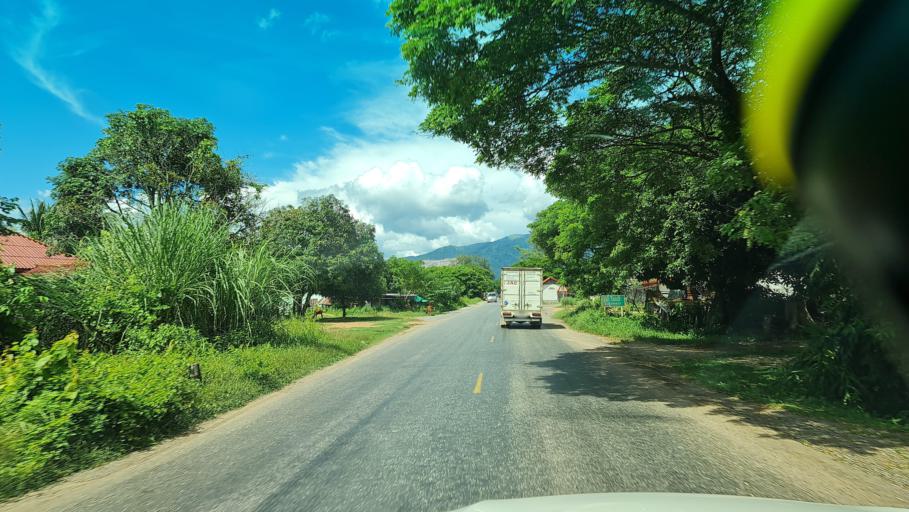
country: LA
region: Bolikhamxai
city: Pakkading
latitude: 18.2966
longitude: 104.0900
